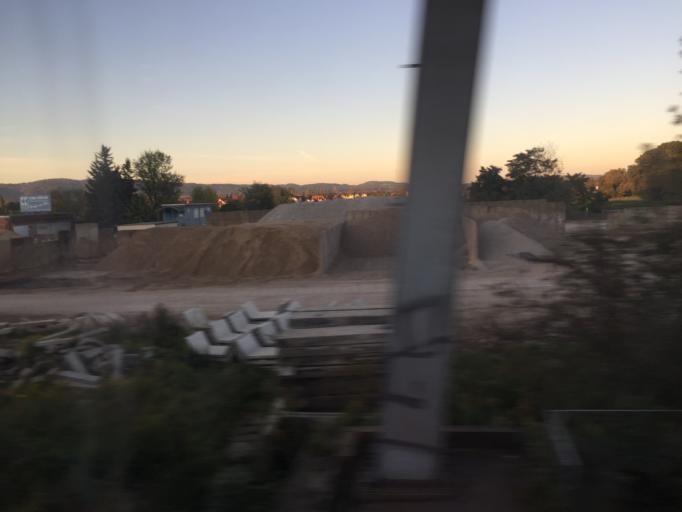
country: DE
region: Saxony
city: Heidenau
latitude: 50.9641
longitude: 13.8879
